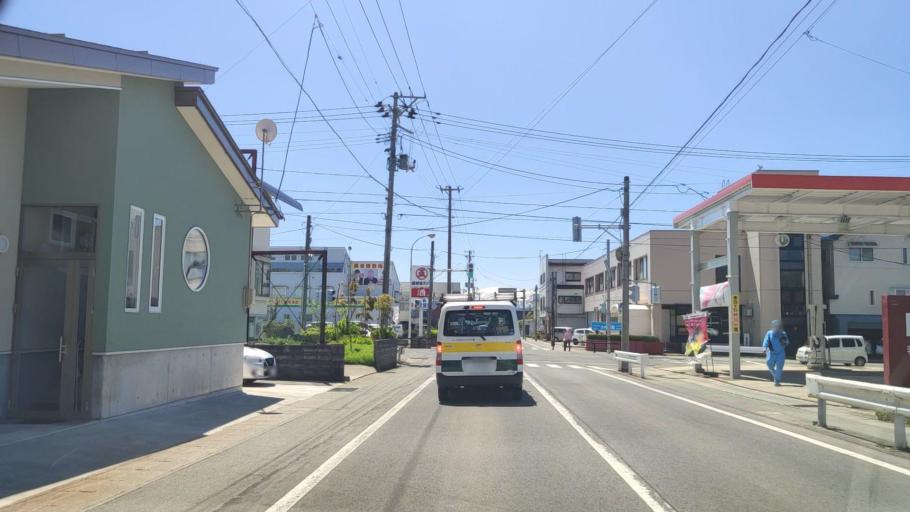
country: JP
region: Yamagata
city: Shinjo
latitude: 38.7602
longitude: 140.3011
